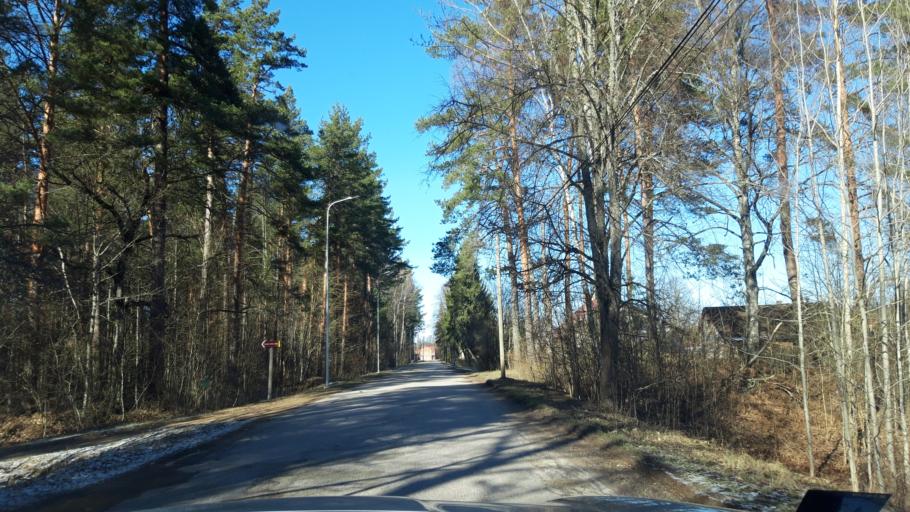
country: LV
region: Strenci
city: Strenci
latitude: 57.6212
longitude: 25.6992
